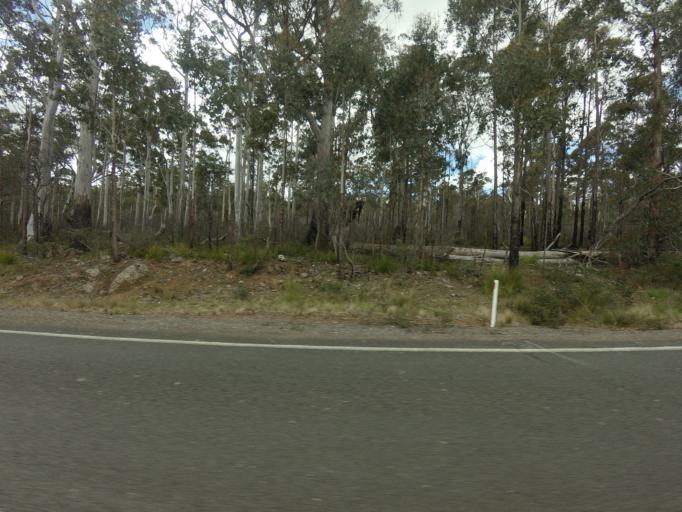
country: AU
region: Tasmania
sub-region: Northern Midlands
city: Evandale
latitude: -41.9906
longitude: 147.7094
